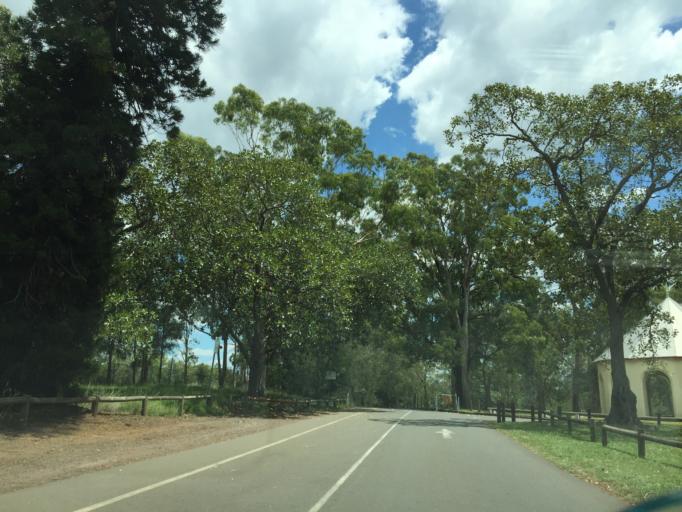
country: AU
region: New South Wales
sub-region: Parramatta
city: City of Parramatta
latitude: -33.8125
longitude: 150.9951
